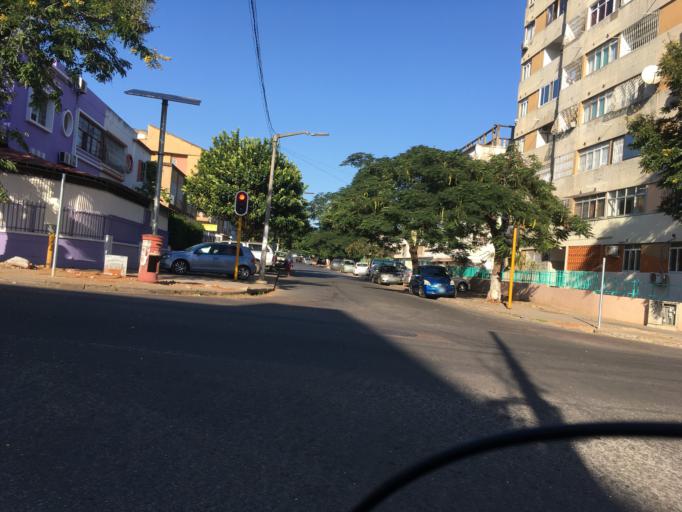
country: MZ
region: Maputo City
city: Maputo
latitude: -25.9603
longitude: 32.5806
